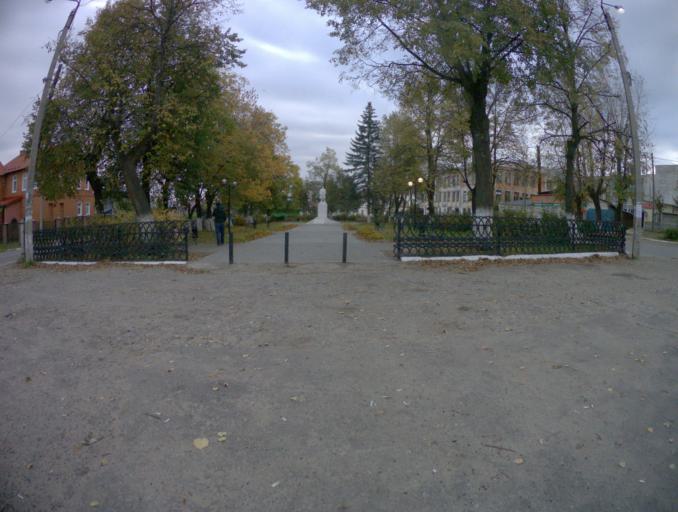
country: RU
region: Vladimir
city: Mstera
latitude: 56.3743
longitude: 41.9398
